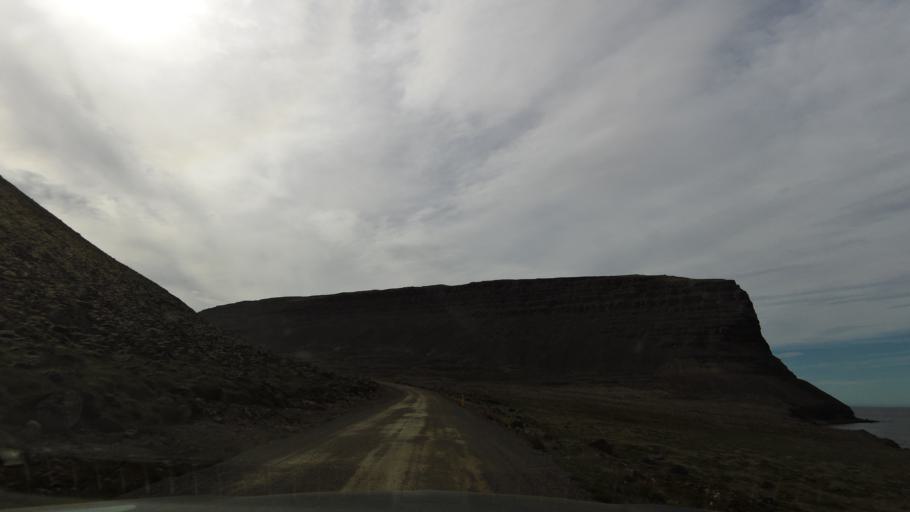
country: IS
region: West
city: Olafsvik
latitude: 65.5767
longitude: -24.0728
